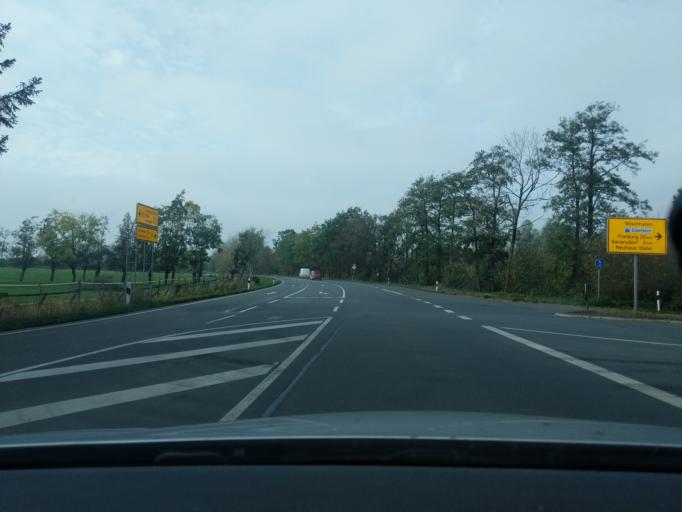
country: DE
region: Lower Saxony
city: Neuhaus an der Oste
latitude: 53.7969
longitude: 9.0496
